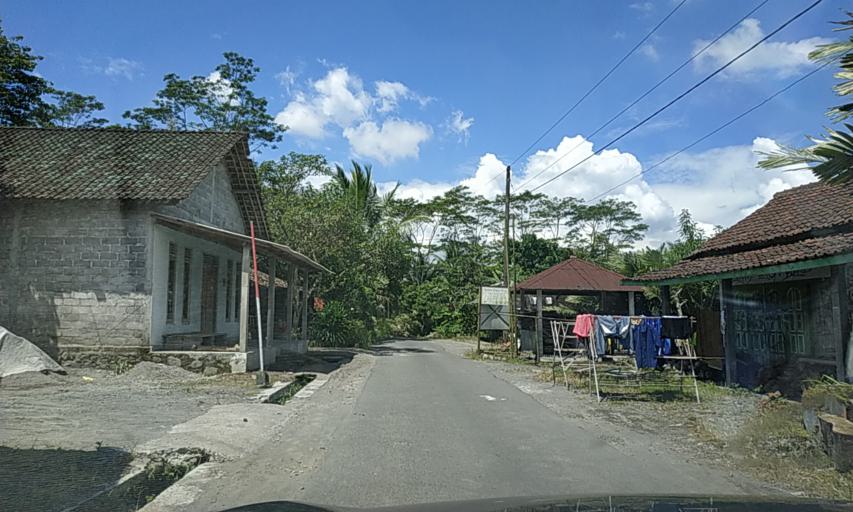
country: ID
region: Central Java
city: Muntilan
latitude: -7.5978
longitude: 110.3531
